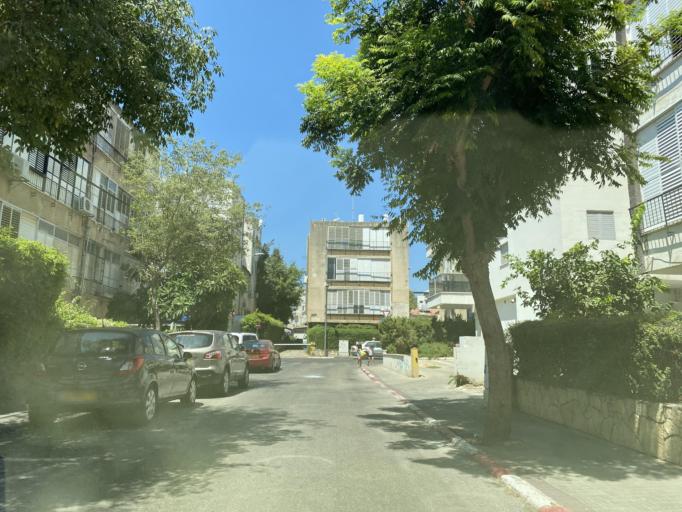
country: IL
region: Tel Aviv
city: Herzliyya
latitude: 32.1661
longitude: 34.8439
